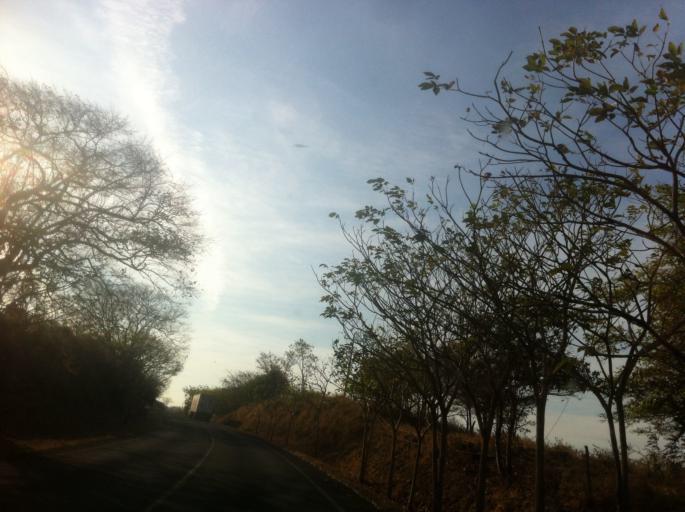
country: NI
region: Rivas
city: Cardenas
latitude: 11.2876
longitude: -85.6777
